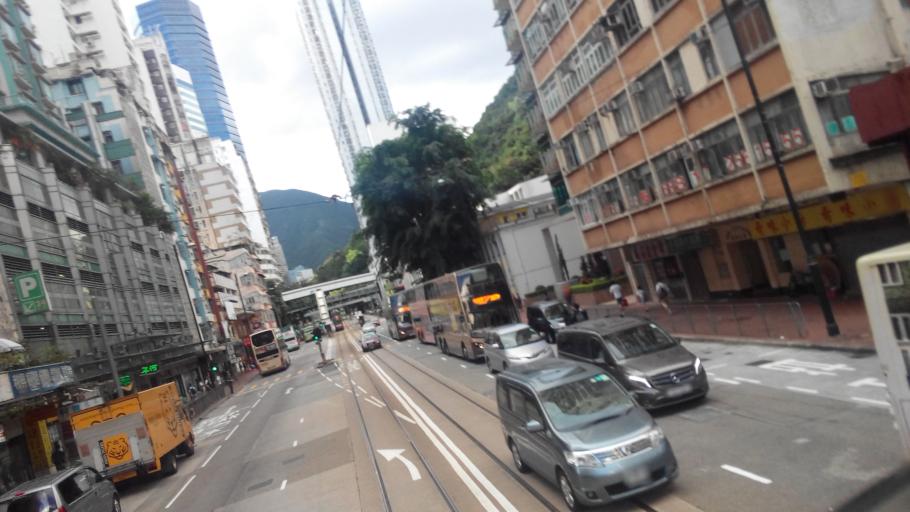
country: HK
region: Kowloon City
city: Kowloon
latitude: 22.2902
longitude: 114.2093
